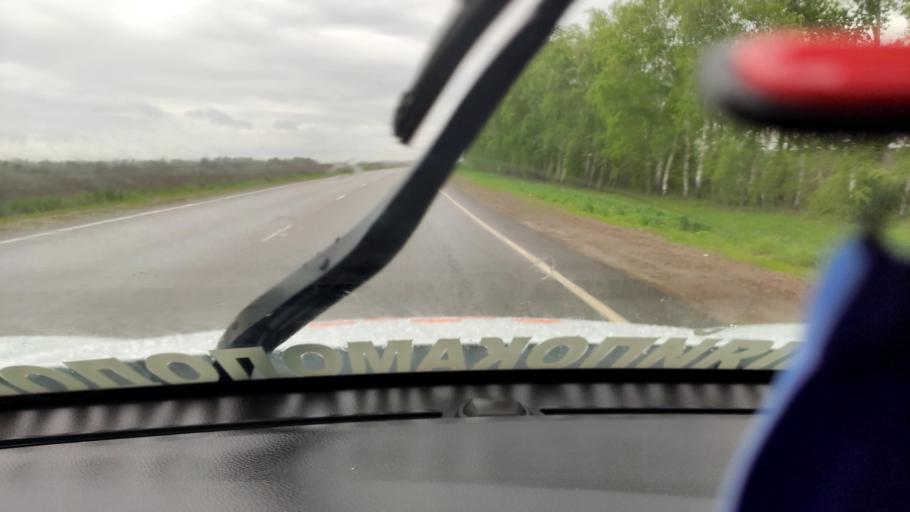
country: RU
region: Voronezj
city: Sredniy Ikorets
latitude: 51.0419
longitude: 39.6898
